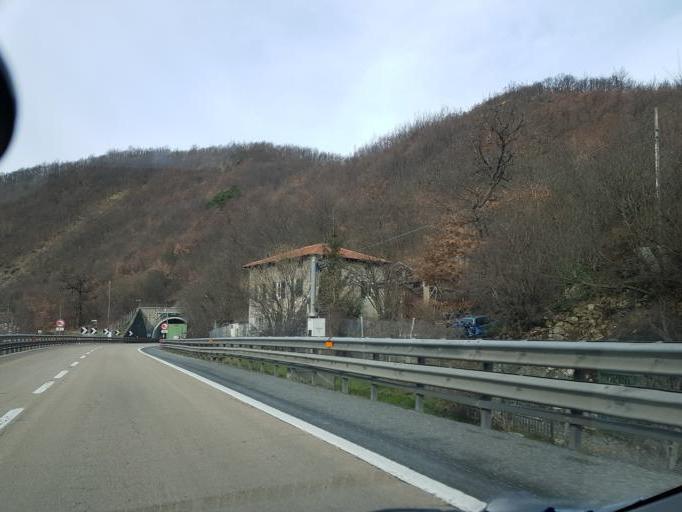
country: IT
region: Liguria
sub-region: Provincia di Genova
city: Isola del Cantone
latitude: 44.6512
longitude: 8.9573
